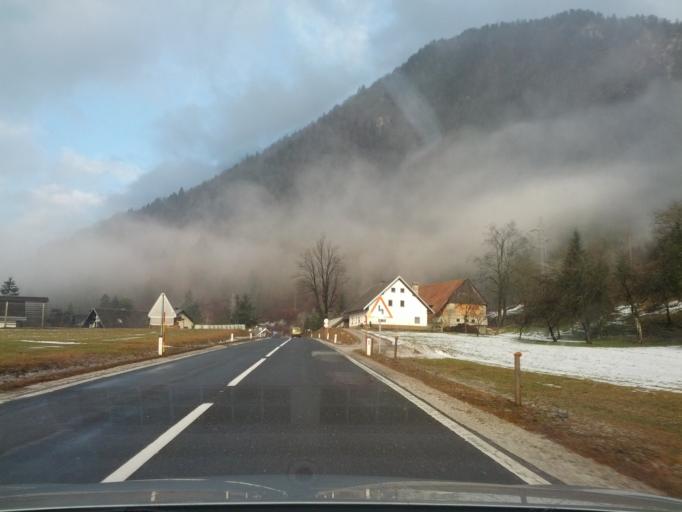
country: SI
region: Kranjska Gora
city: Mojstrana
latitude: 46.4749
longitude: 13.9118
